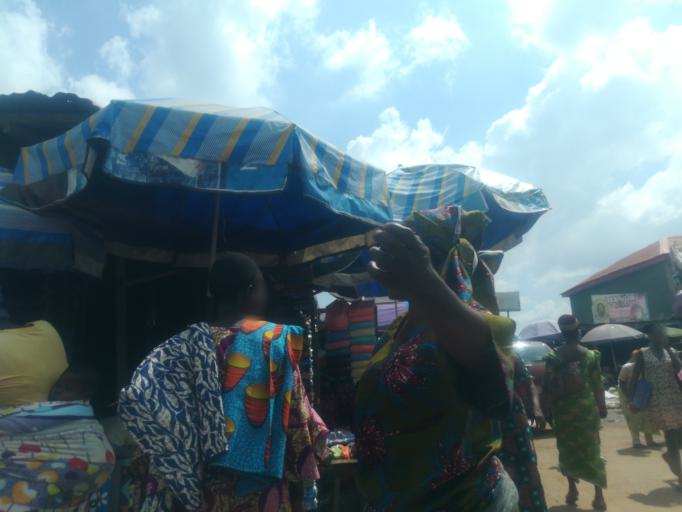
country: NG
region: Oyo
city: Ibadan
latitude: 7.3934
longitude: 3.9576
